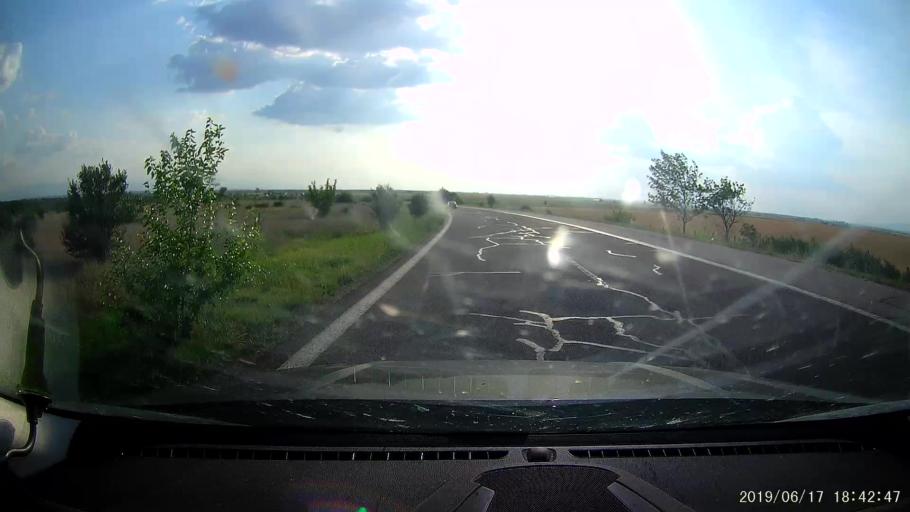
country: BG
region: Stara Zagora
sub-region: Obshtina Chirpan
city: Chirpan
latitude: 42.1950
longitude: 25.2302
